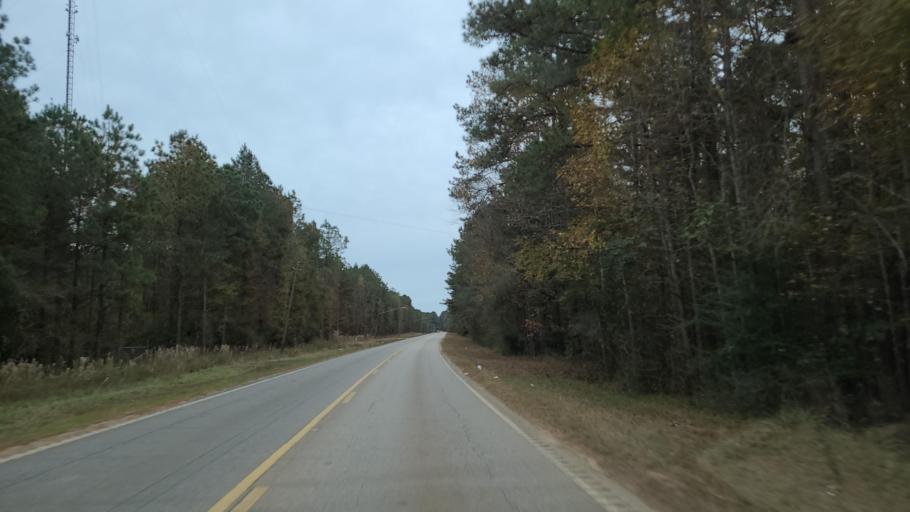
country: US
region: Mississippi
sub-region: Clarke County
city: Stonewall
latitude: 32.0566
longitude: -88.9004
